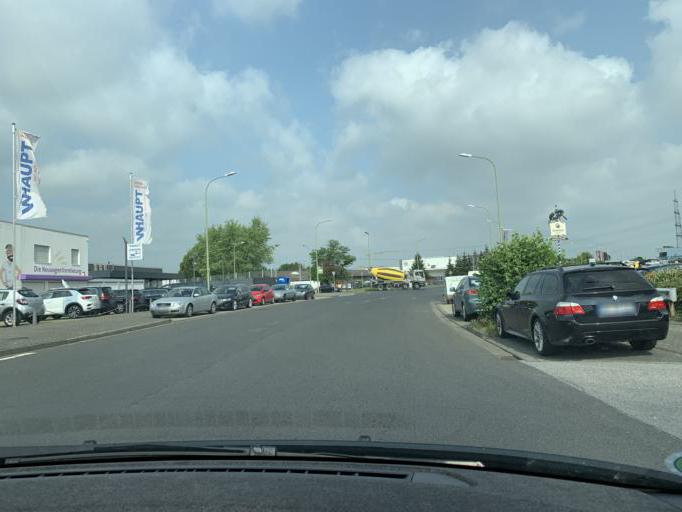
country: DE
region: North Rhine-Westphalia
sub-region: Regierungsbezirk Koln
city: Dueren
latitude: 50.8339
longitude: 6.4628
